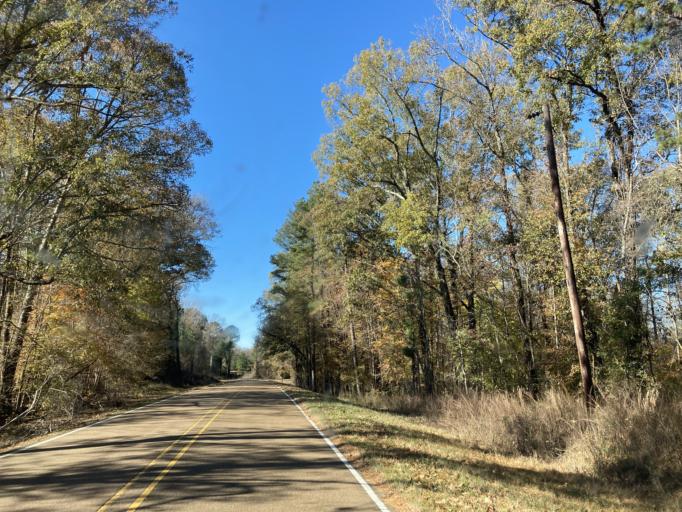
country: US
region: Mississippi
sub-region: Hinds County
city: Lynchburg
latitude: 32.5958
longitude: -90.5388
